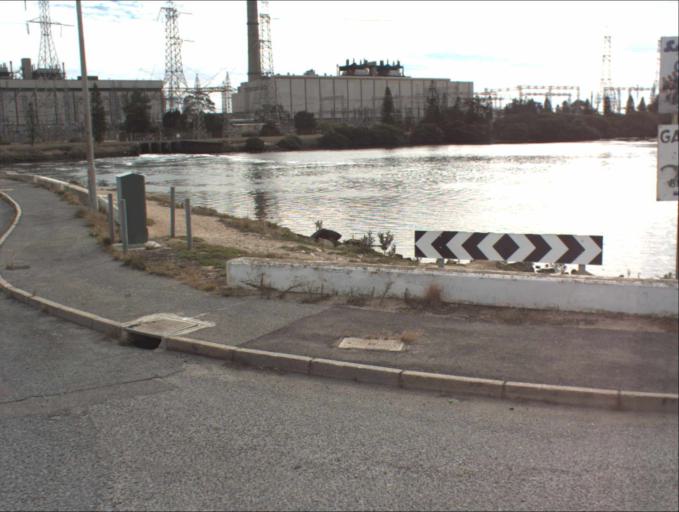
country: AU
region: South Australia
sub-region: Port Adelaide Enfield
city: Birkenhead
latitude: -34.8101
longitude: 138.5253
